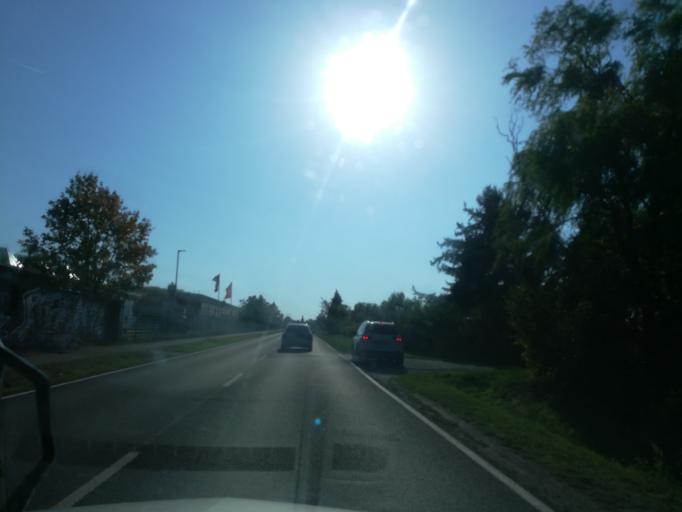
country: DE
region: Saxony-Anhalt
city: Gommern
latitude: 52.0807
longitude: 11.8170
